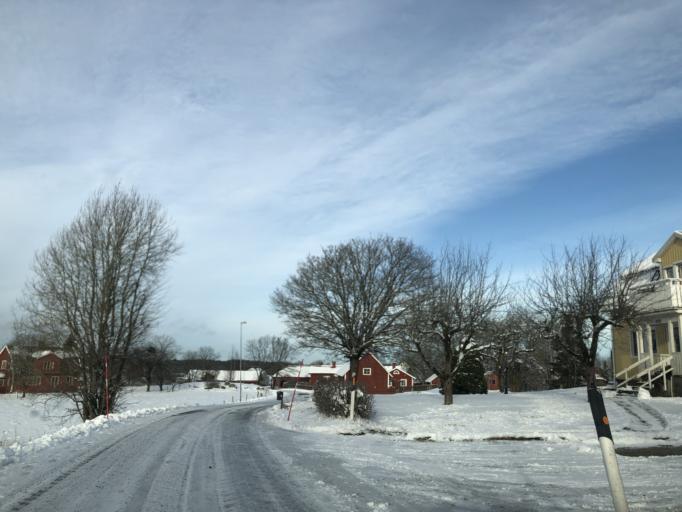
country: SE
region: Vaestra Goetaland
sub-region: Ulricehamns Kommun
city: Ulricehamn
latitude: 57.7804
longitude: 13.5241
